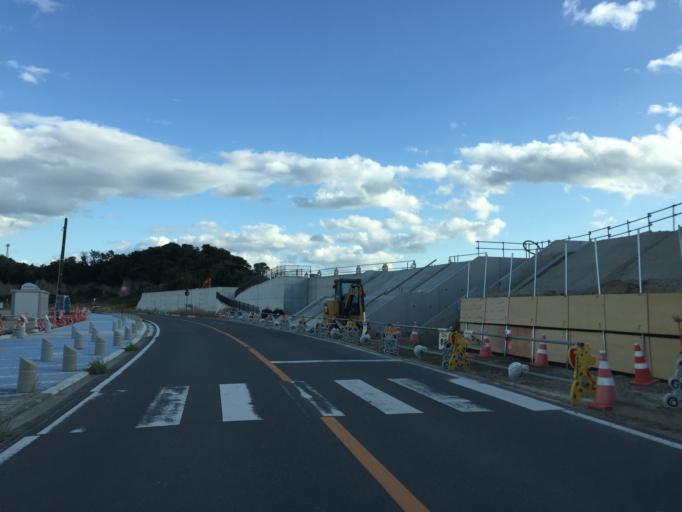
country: JP
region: Miyagi
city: Marumori
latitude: 37.8281
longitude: 140.9658
